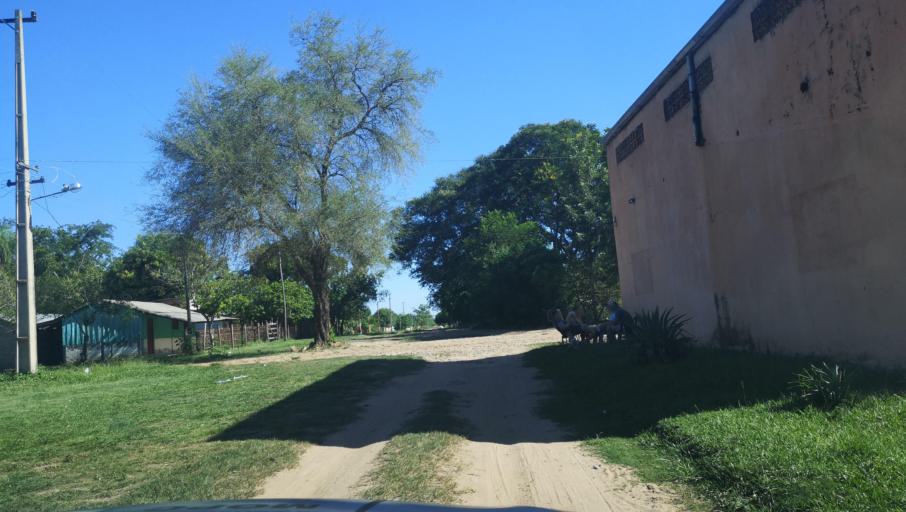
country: PY
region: Caaguazu
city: Carayao
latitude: -25.1941
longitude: -56.3980
